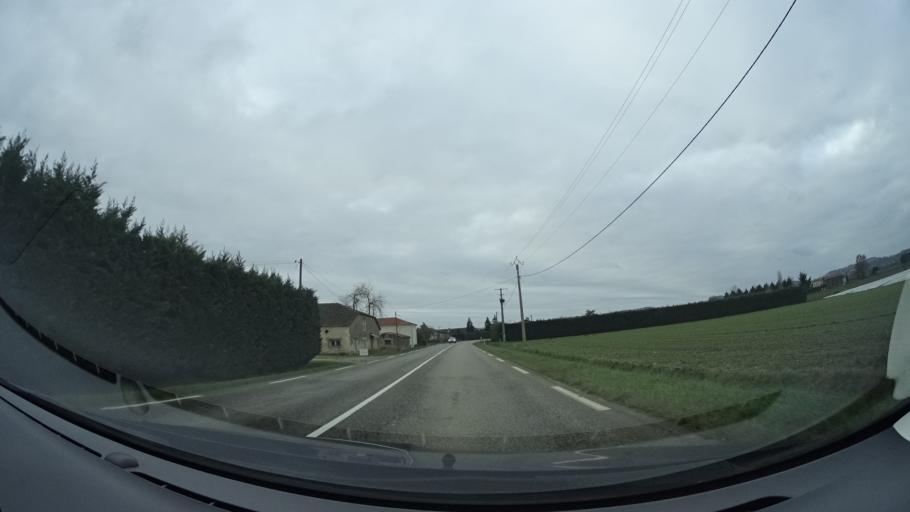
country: FR
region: Aquitaine
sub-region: Departement du Lot-et-Garonne
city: Clairac
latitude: 44.3466
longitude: 0.4134
